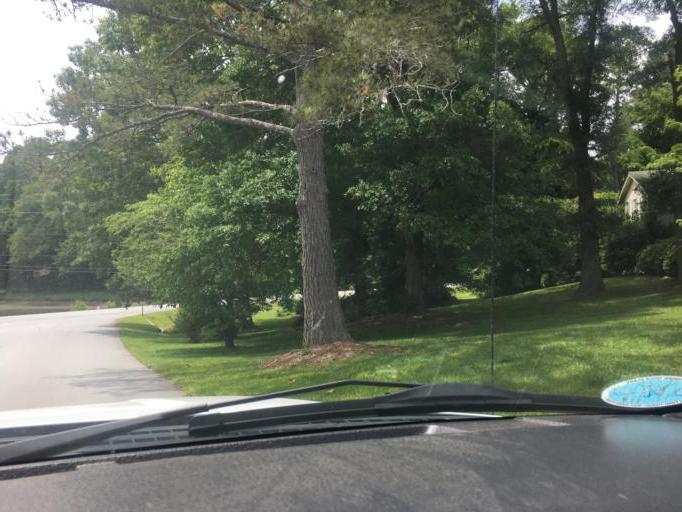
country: US
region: Georgia
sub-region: Rockdale County
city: Lakeview Estates
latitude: 33.7172
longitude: -84.0580
